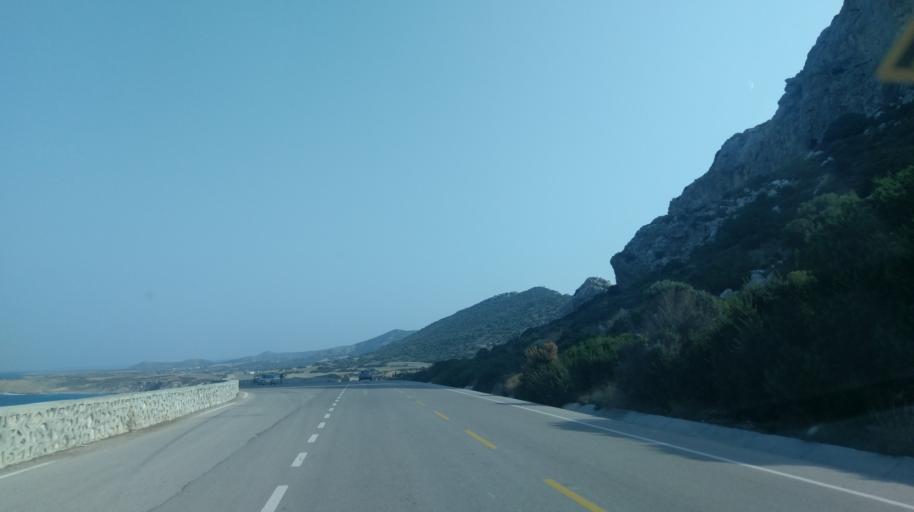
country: CY
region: Ammochostos
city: Leonarisso
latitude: 35.4708
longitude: 34.0390
